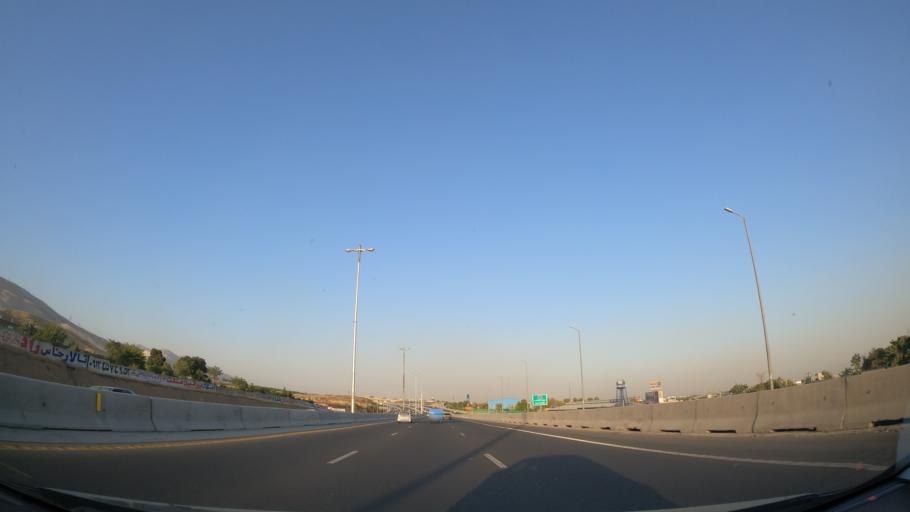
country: IR
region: Tehran
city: Shahr-e Qods
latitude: 35.7422
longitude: 51.1126
